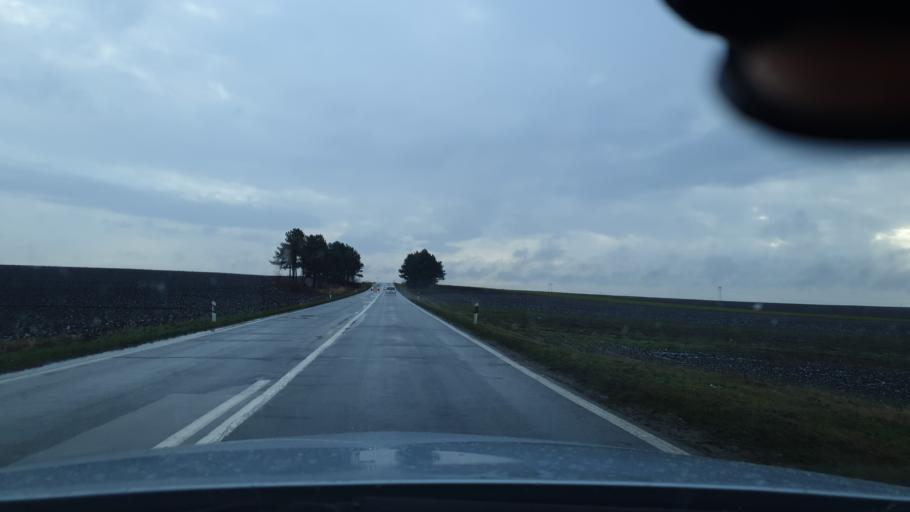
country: RS
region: Autonomna Pokrajina Vojvodina
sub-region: Juznobanatski Okrug
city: Kovin
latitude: 44.8317
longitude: 20.8287
